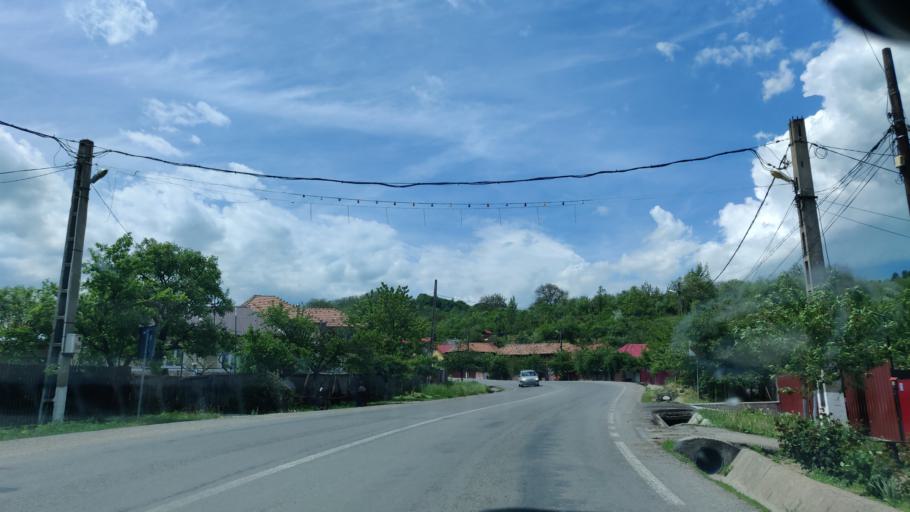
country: RO
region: Vrancea
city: Matacina
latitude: 45.8914
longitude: 26.8403
